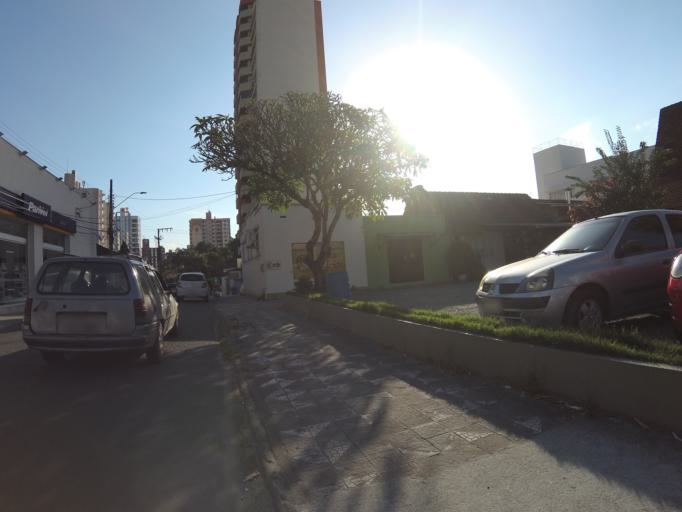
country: BR
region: Santa Catarina
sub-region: Blumenau
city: Blumenau
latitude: -26.9069
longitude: -49.0746
